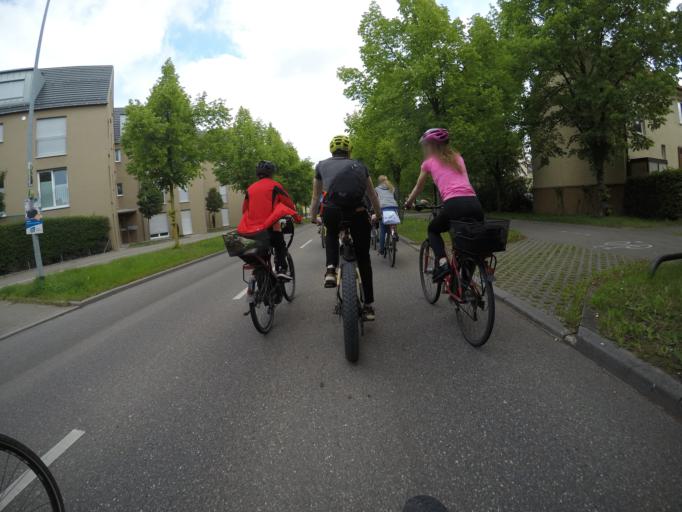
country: DE
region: Baden-Wuerttemberg
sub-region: Regierungsbezirk Stuttgart
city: Korntal
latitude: 48.8115
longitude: 9.1095
